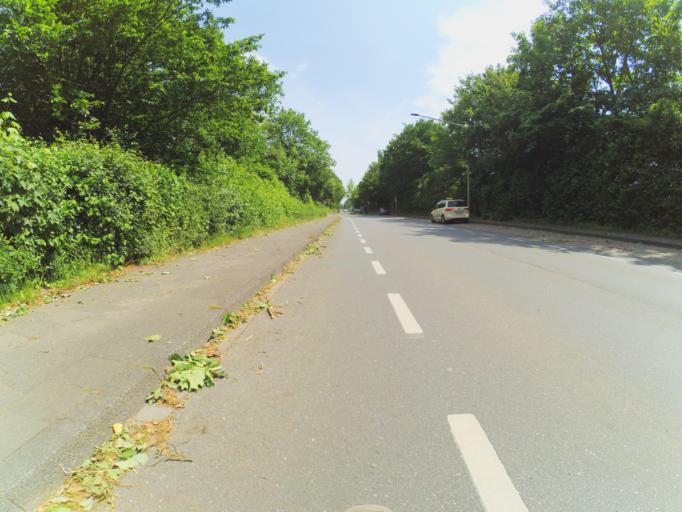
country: DE
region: North Rhine-Westphalia
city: Ibbenburen
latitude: 52.2816
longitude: 7.7139
